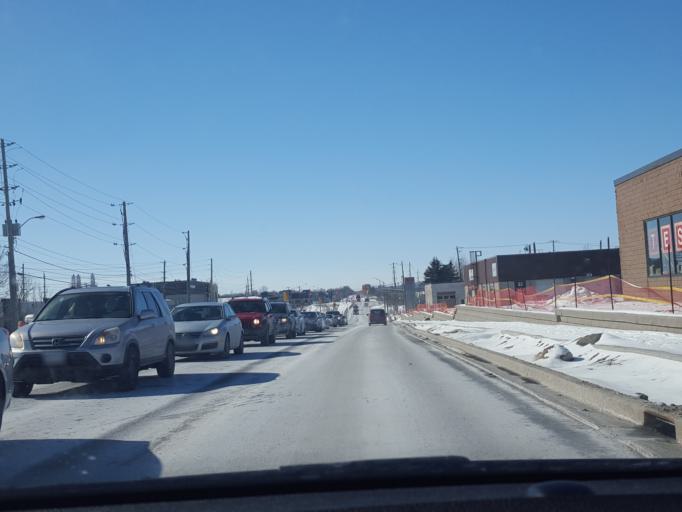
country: CA
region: Ontario
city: Waterloo
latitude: 43.5010
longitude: -80.5354
